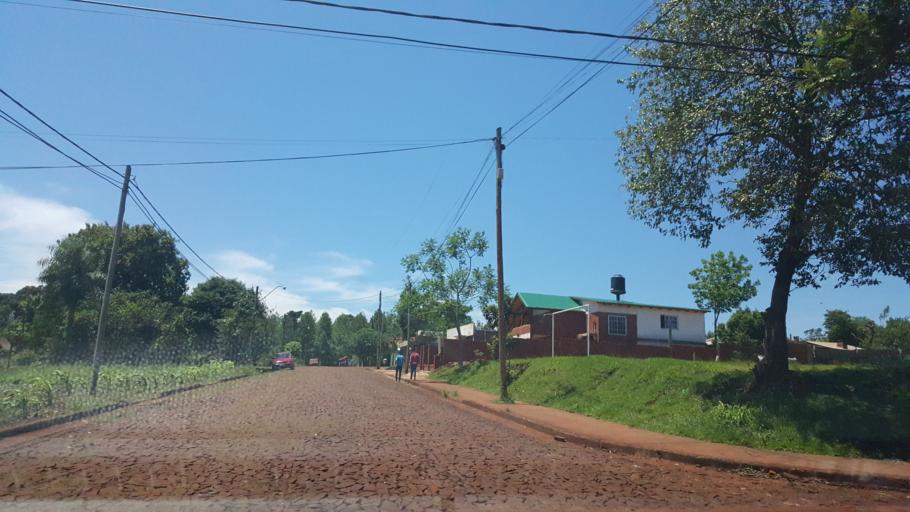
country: AR
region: Misiones
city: Capiovi
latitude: -26.9284
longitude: -55.0518
